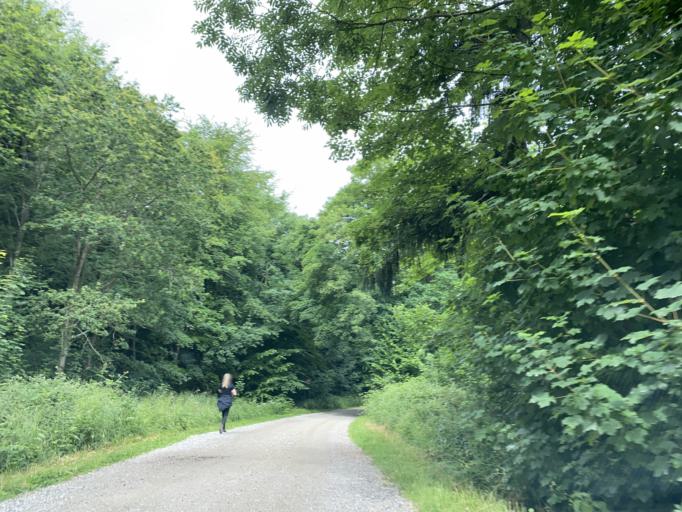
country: DK
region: South Denmark
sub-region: Sonderborg Kommune
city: Sonderborg
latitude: 54.9018
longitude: 9.8391
